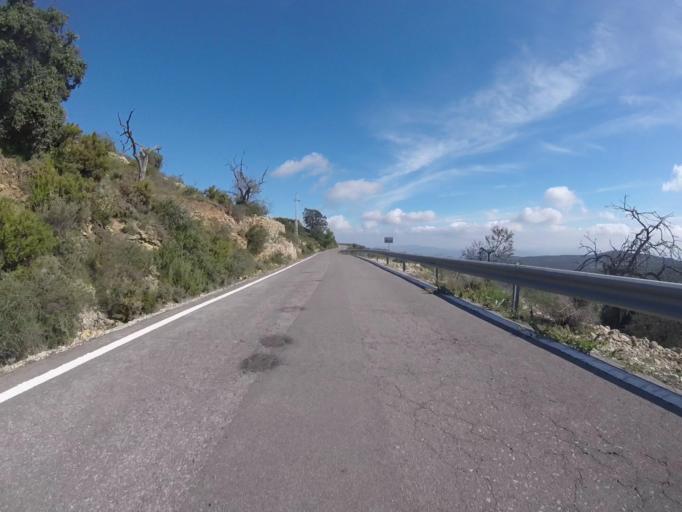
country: ES
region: Valencia
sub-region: Provincia de Castello
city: Sarratella
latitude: 40.3271
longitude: 0.0290
